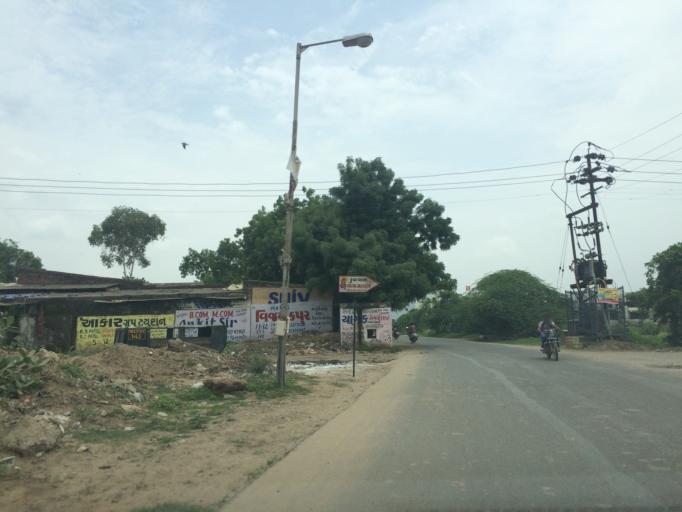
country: IN
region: Gujarat
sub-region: Ahmadabad
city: Ahmedabad
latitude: 23.0883
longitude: 72.5651
